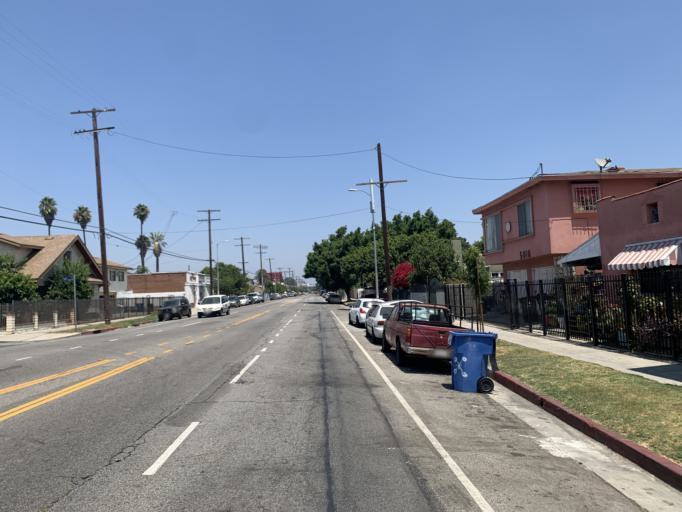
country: US
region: California
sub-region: Los Angeles County
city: Florence-Graham
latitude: 33.9968
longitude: -118.2870
